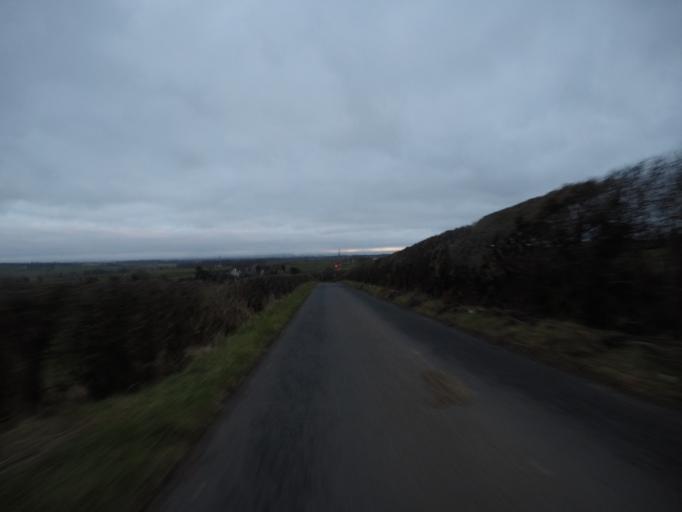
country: GB
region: Scotland
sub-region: North Ayrshire
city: Kilwinning
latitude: 55.6767
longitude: -4.7244
